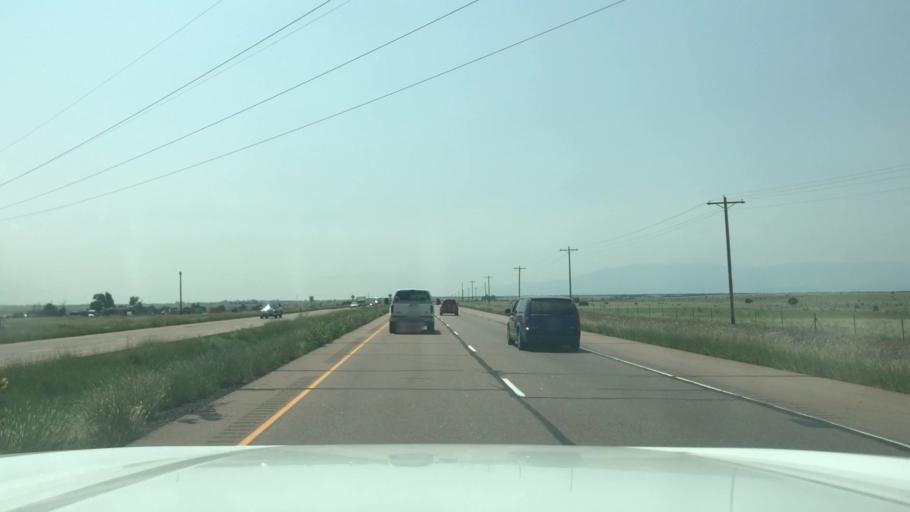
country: US
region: Colorado
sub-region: Pueblo County
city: Pueblo
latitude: 38.1011
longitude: -104.6854
